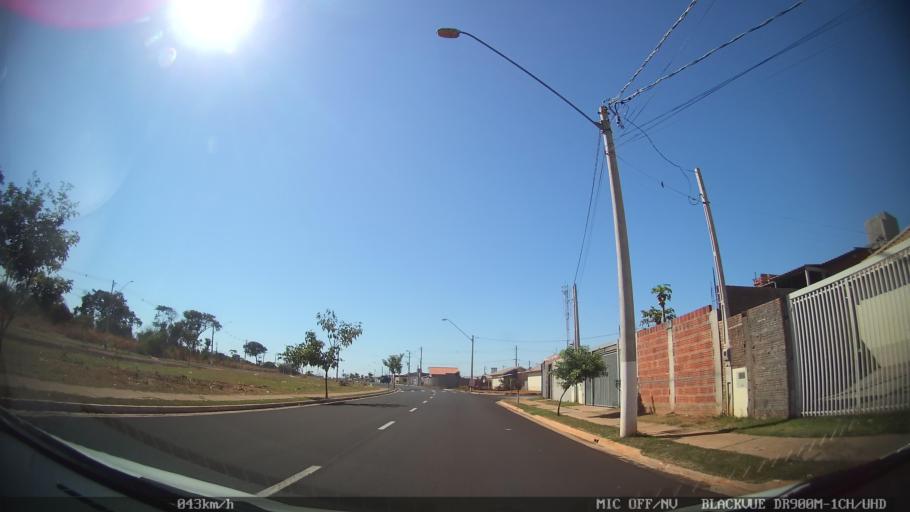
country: BR
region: Sao Paulo
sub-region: Sao Jose Do Rio Preto
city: Sao Jose do Rio Preto
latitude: -20.7502
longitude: -49.4396
